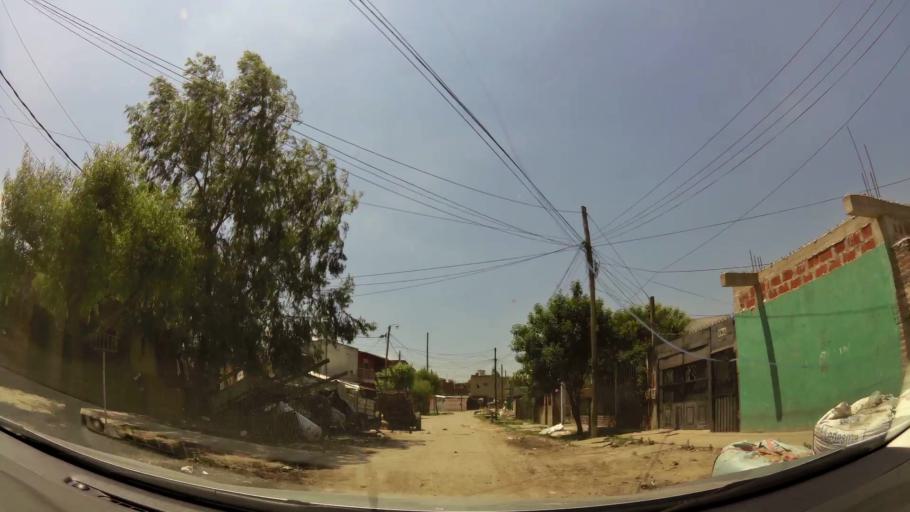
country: AR
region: Buenos Aires
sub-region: Partido de Tigre
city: Tigre
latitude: -34.4559
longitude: -58.5991
